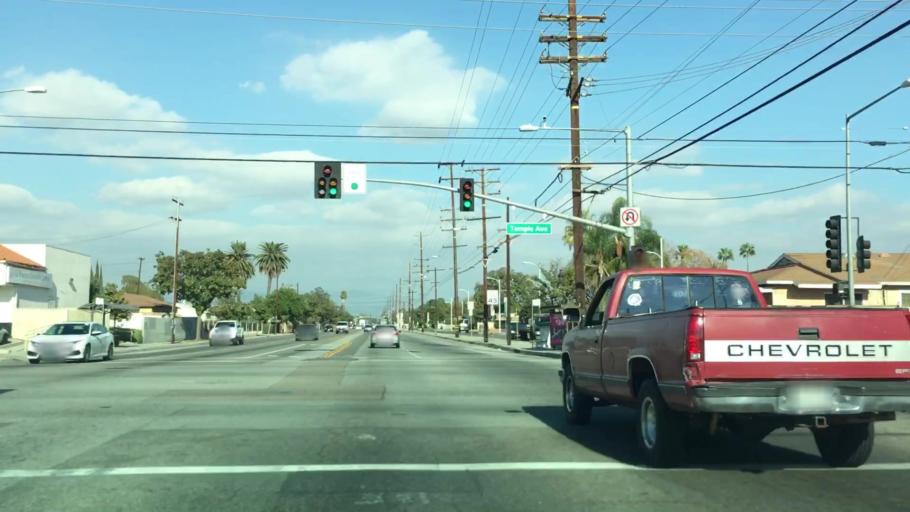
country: US
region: California
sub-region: Los Angeles County
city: West Puente Valley
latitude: 34.0406
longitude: -117.9682
